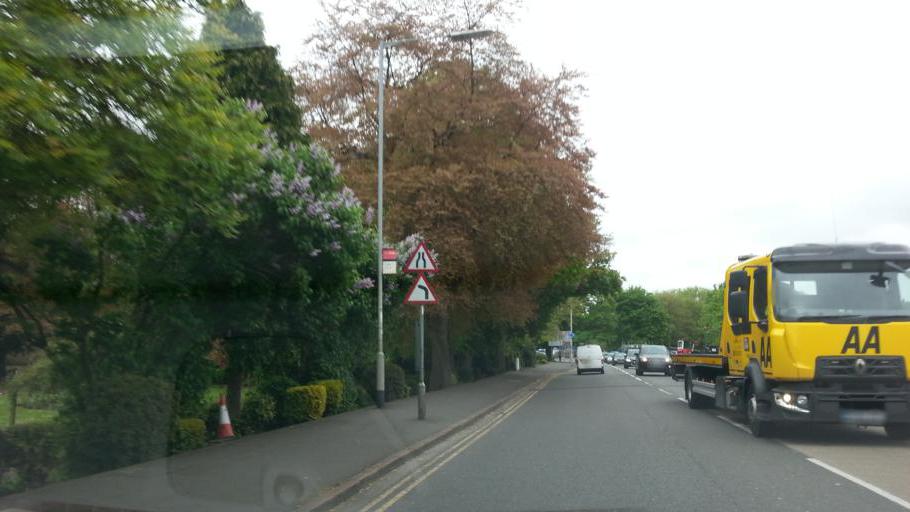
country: GB
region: England
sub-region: Peterborough
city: Peterborough
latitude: 52.5705
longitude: -0.2393
